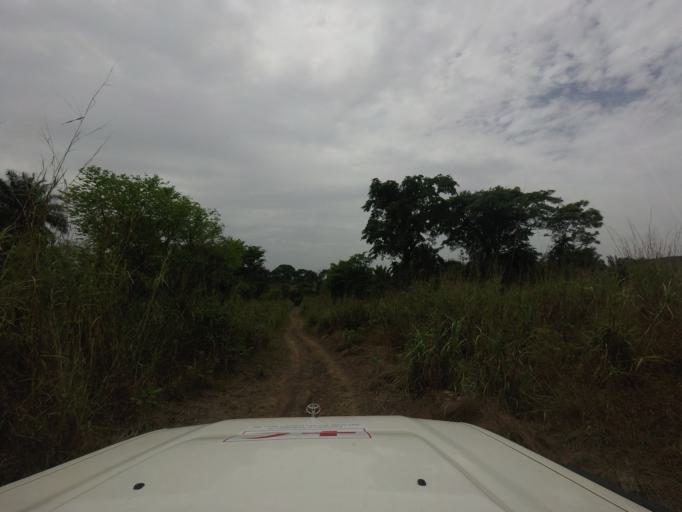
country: SL
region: Eastern Province
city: Buedu
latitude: 8.4272
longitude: -10.2635
